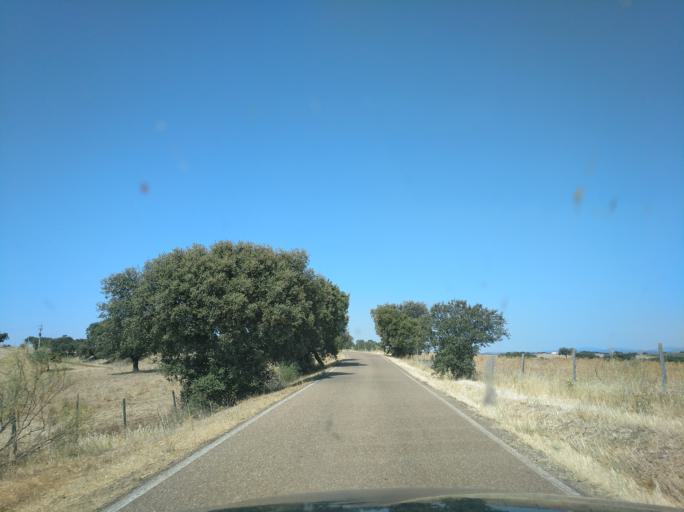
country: PT
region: Portalegre
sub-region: Campo Maior
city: Campo Maior
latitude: 39.0474
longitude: -7.0106
